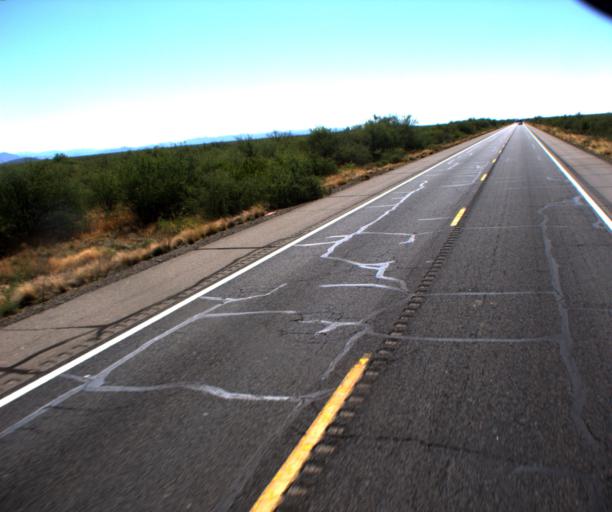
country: US
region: Arizona
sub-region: Yavapai County
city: Congress
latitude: 34.1165
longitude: -112.9406
